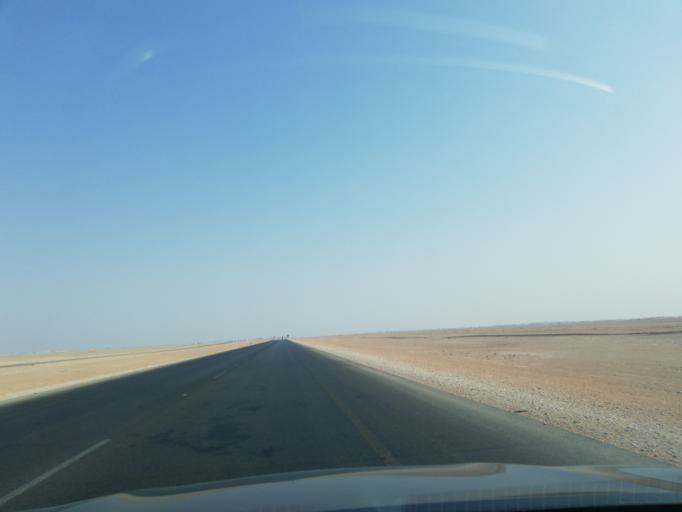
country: OM
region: Zufar
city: Salalah
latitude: 17.7436
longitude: 54.0202
